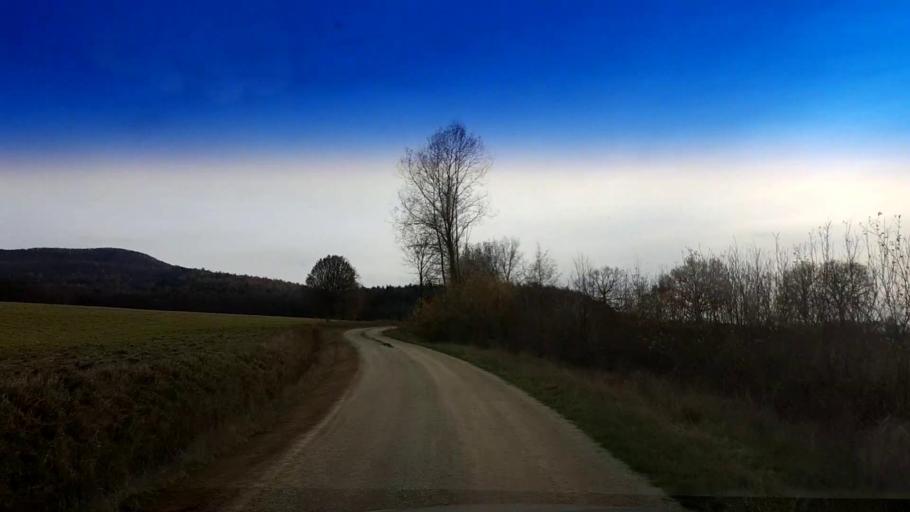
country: DE
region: Bavaria
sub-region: Upper Franconia
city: Schesslitz
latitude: 49.9522
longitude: 11.0157
